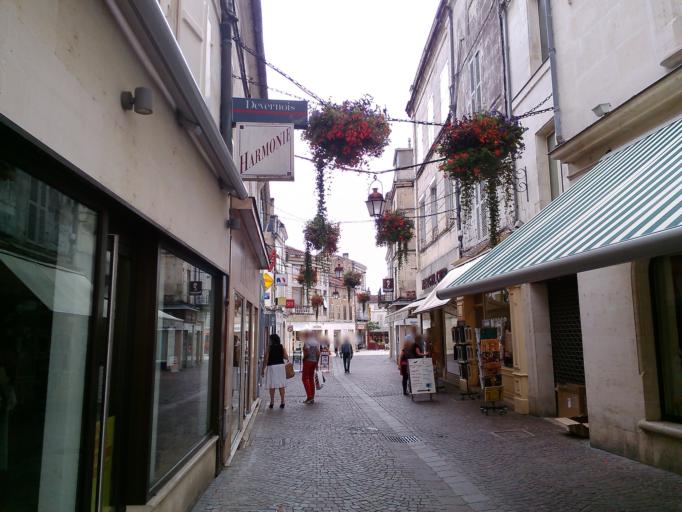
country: FR
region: Poitou-Charentes
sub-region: Departement de la Charente
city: Cognac
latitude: 45.6954
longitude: -0.3280
